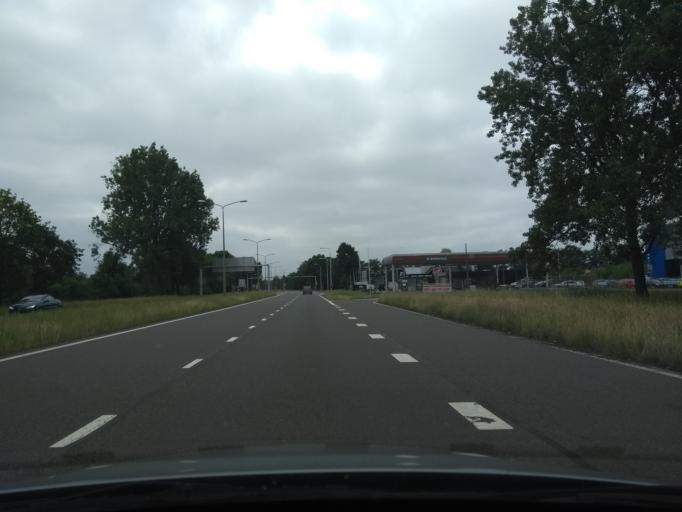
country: NL
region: Overijssel
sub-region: Gemeente Wierden
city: Wierden
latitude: 52.3534
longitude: 6.6244
